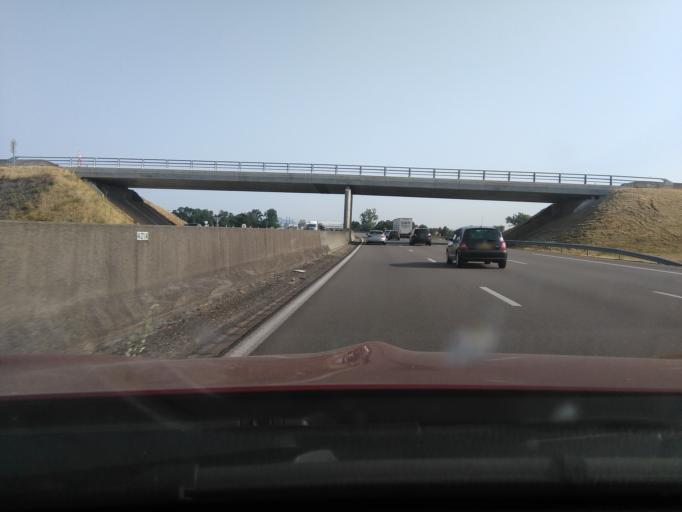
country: FR
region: Rhone-Alpes
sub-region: Departement du Rhone
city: Arnas
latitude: 46.0240
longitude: 4.7249
